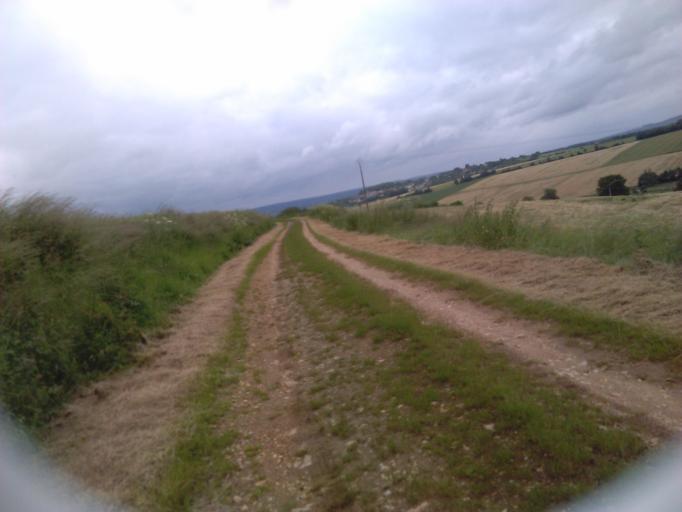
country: FR
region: Centre
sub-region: Departement du Cher
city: Sancerre
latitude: 47.3125
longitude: 2.7270
